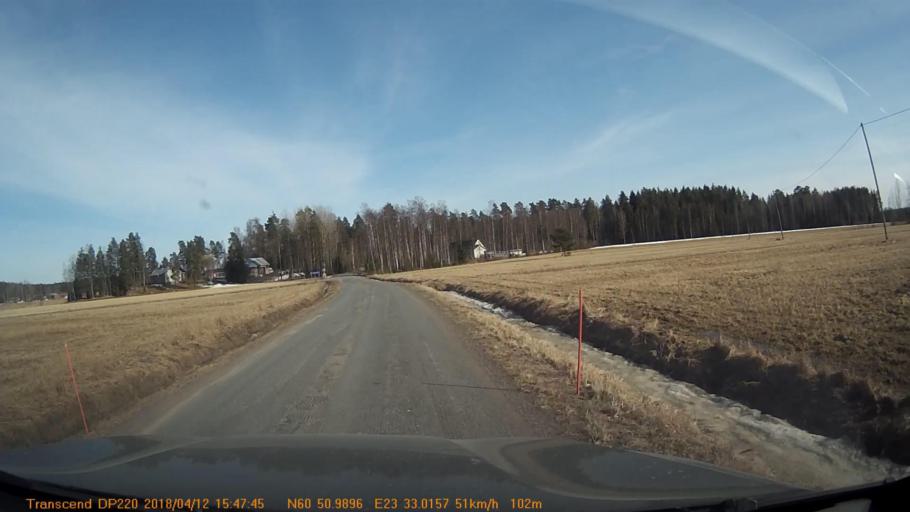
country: FI
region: Haeme
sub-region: Forssa
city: Forssa
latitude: 60.8497
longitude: 23.5506
